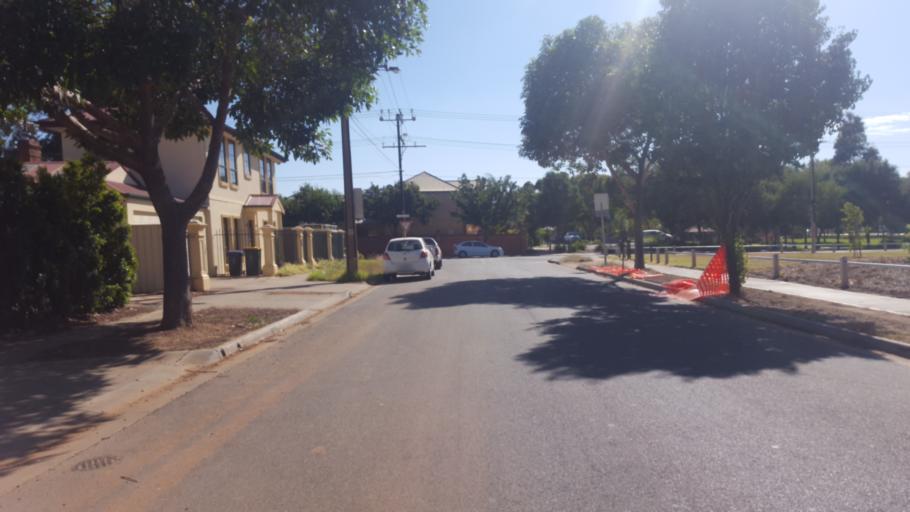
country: AU
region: South Australia
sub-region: Charles Sturt
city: Allenby Gardens
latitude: -34.8954
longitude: 138.5730
